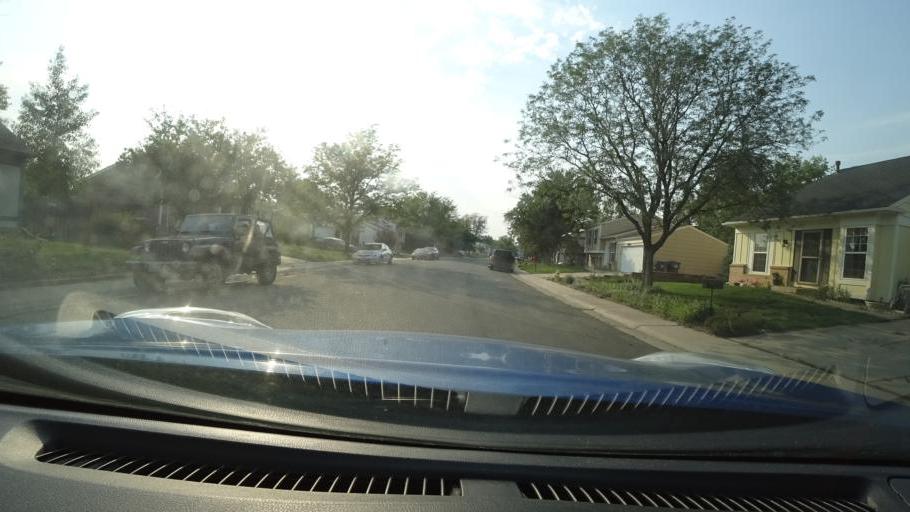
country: US
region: Colorado
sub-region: Adams County
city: Aurora
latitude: 39.7421
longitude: -104.7577
